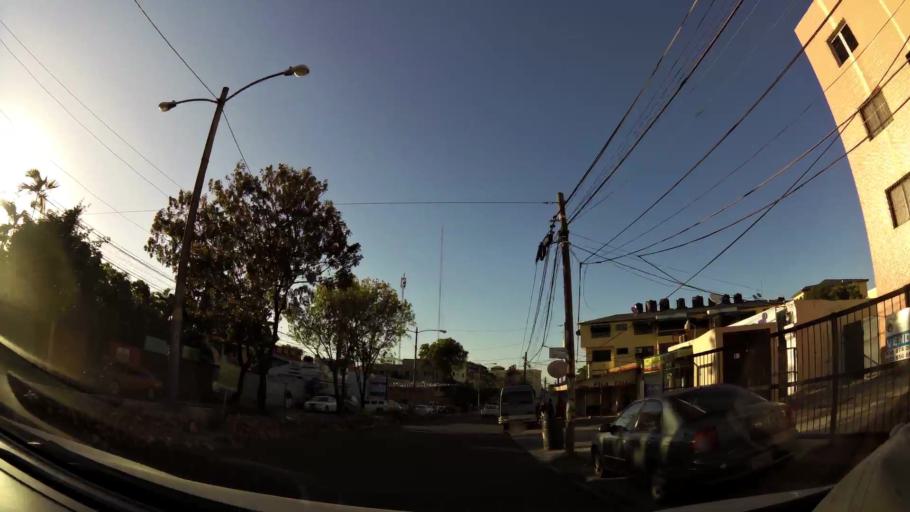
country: DO
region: Nacional
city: Santo Domingo
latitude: 18.4852
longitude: -69.9685
